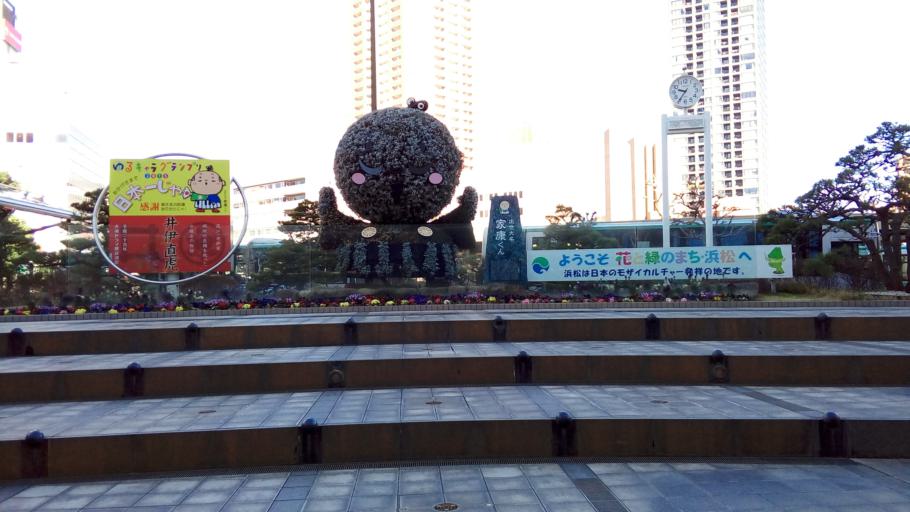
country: JP
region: Shizuoka
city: Hamamatsu
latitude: 34.7050
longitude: 137.7342
